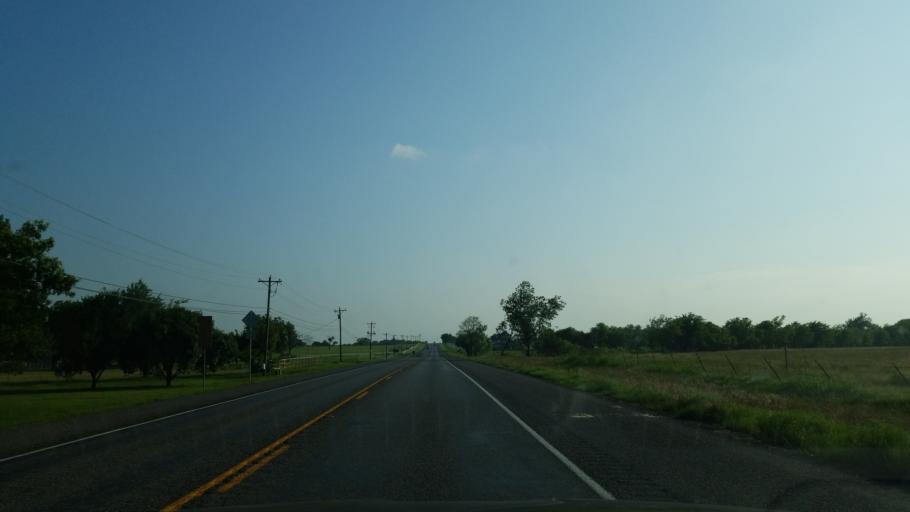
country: US
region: Texas
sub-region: Denton County
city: Krugerville
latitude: 33.3050
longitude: -97.0643
